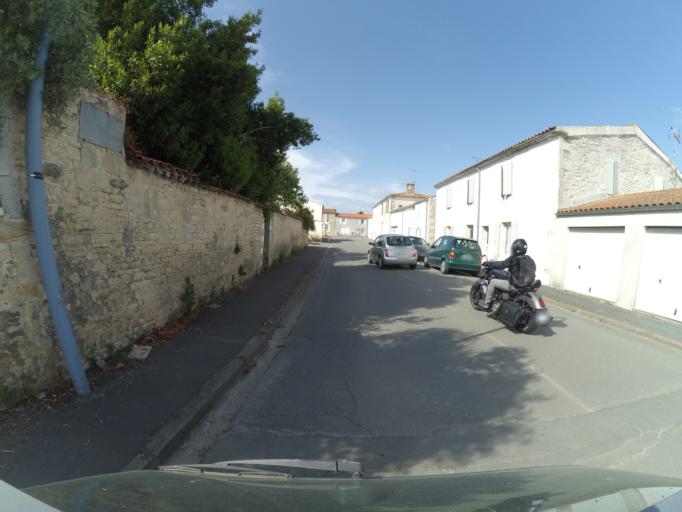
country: FR
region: Poitou-Charentes
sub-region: Departement de la Charente-Maritime
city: Andilly
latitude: 46.2407
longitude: -1.0674
